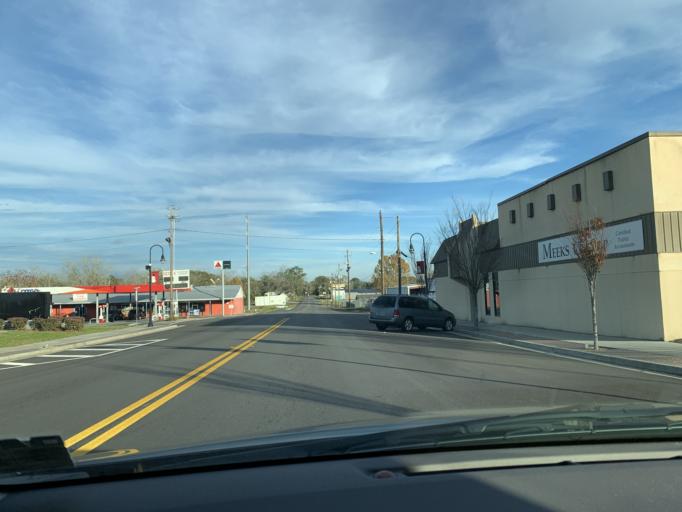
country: US
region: Georgia
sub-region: Irwin County
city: Ocilla
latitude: 31.5942
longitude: -83.2483
